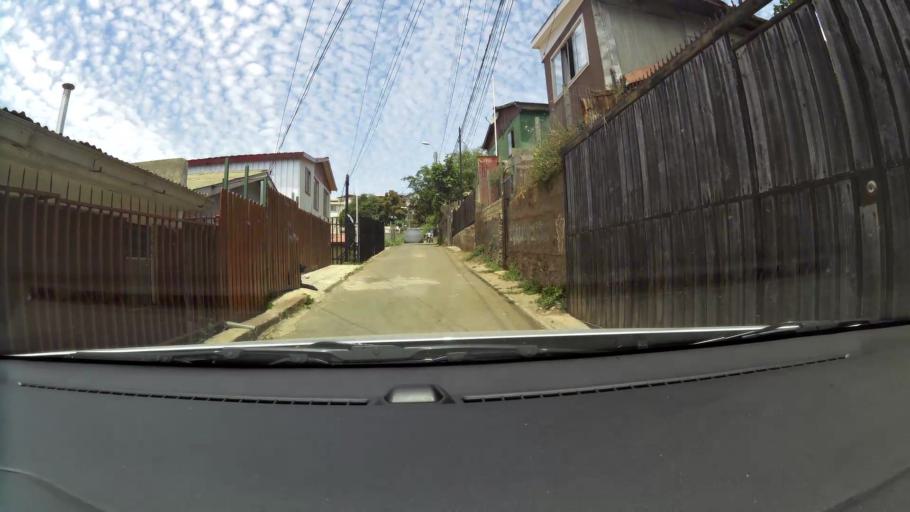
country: CL
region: Valparaiso
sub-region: Provincia de Valparaiso
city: Vina del Mar
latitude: -33.0516
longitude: -71.5661
